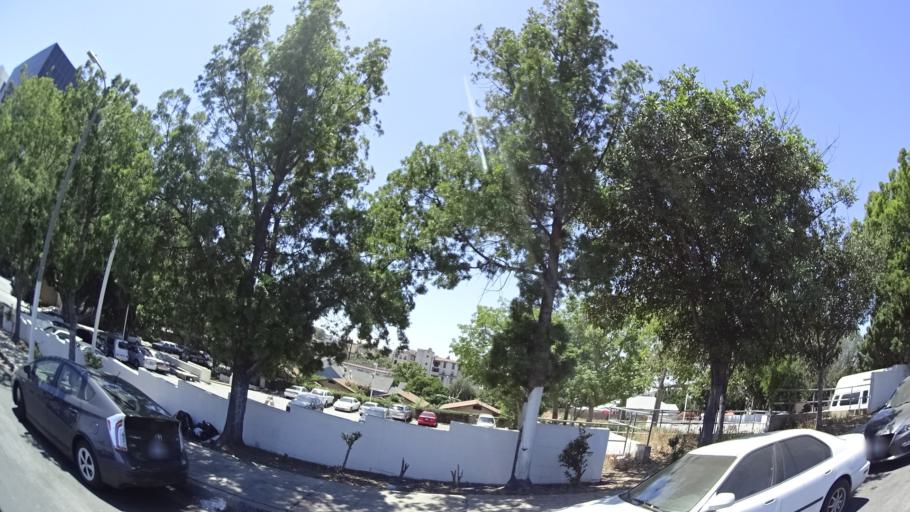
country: US
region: California
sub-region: Los Angeles County
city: Echo Park
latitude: 34.0704
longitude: -118.2642
